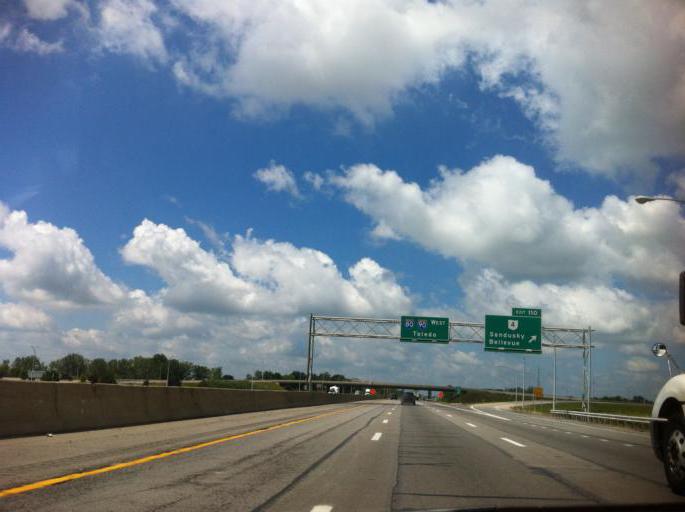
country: US
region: Ohio
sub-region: Huron County
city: Bellevue
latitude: 41.3406
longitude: -82.7617
